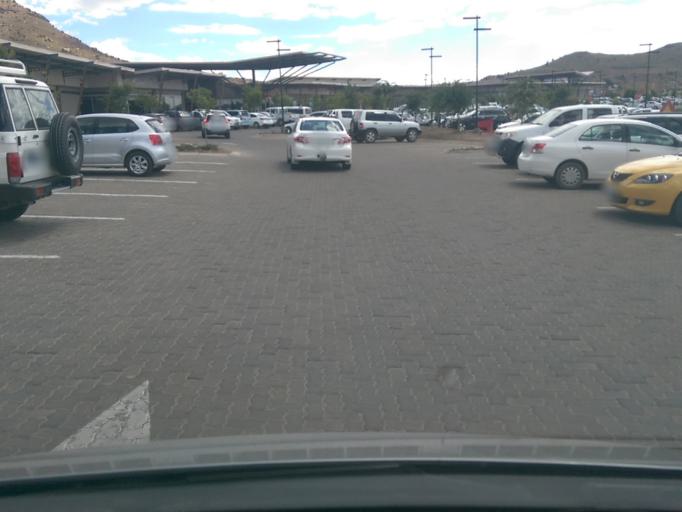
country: LS
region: Maseru
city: Maseru
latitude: -29.3355
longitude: 27.4847
